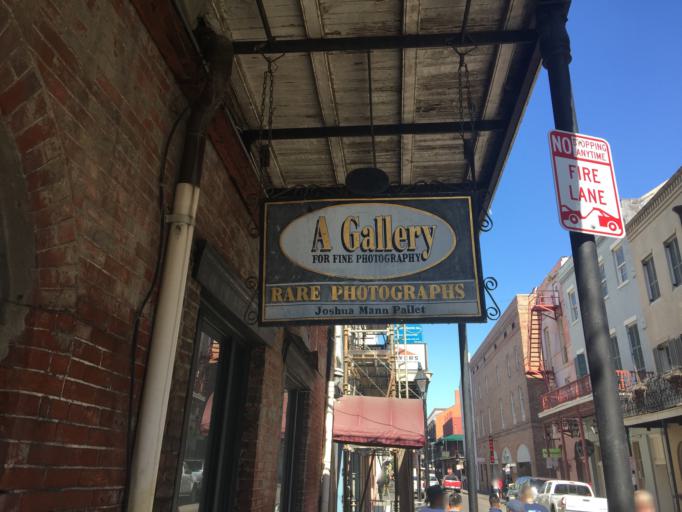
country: US
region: Louisiana
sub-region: Orleans Parish
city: New Orleans
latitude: 29.9544
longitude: -90.0667
